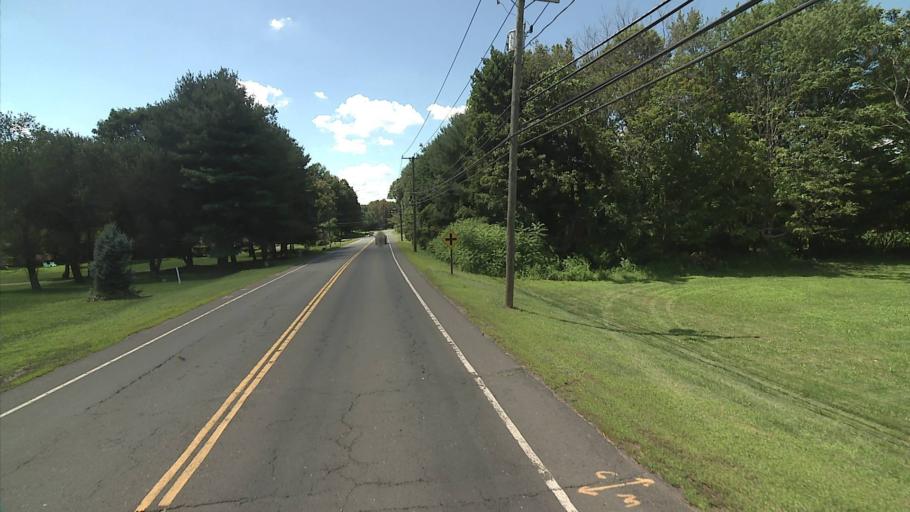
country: US
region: Connecticut
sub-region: Hartford County
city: Suffield Depot
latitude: 41.9832
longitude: -72.6777
